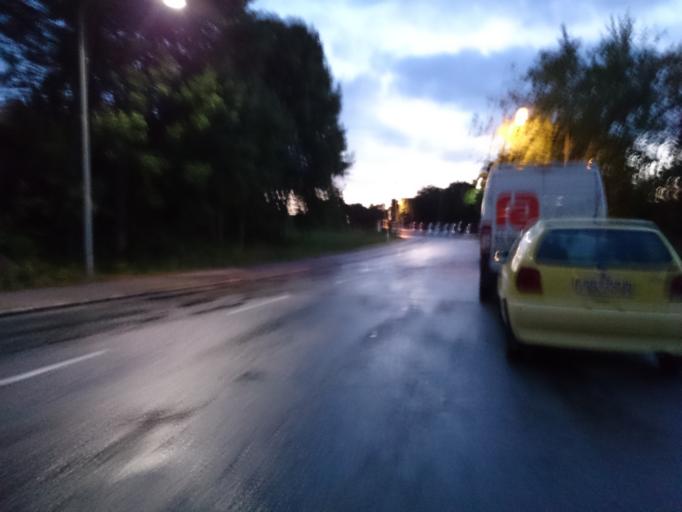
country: SE
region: Stockholm
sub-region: Stockholms Kommun
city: Arsta
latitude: 59.2884
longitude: 18.0373
